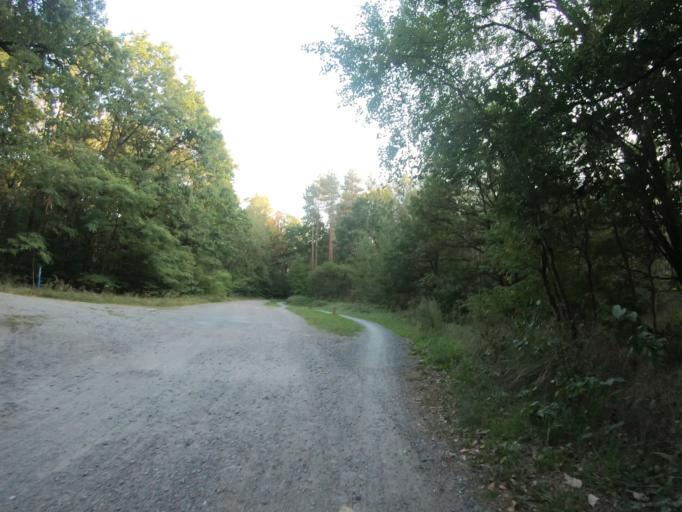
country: DE
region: Lower Saxony
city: Calberlah
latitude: 52.4625
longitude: 10.6204
